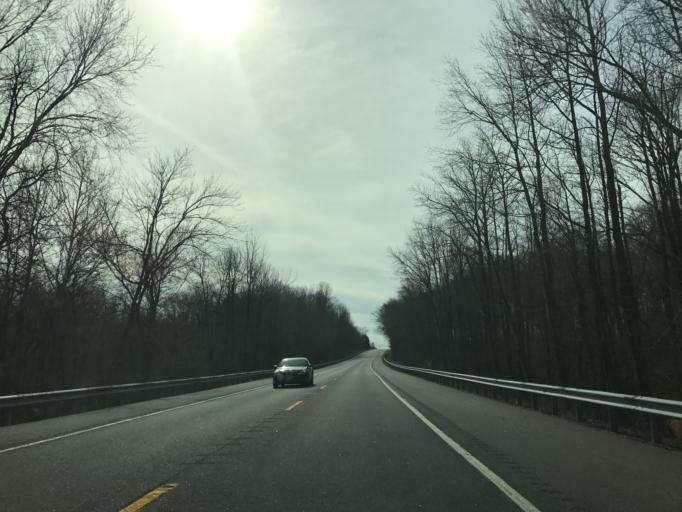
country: US
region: Maryland
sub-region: Queen Anne's County
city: Kingstown
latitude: 39.1426
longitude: -75.9880
